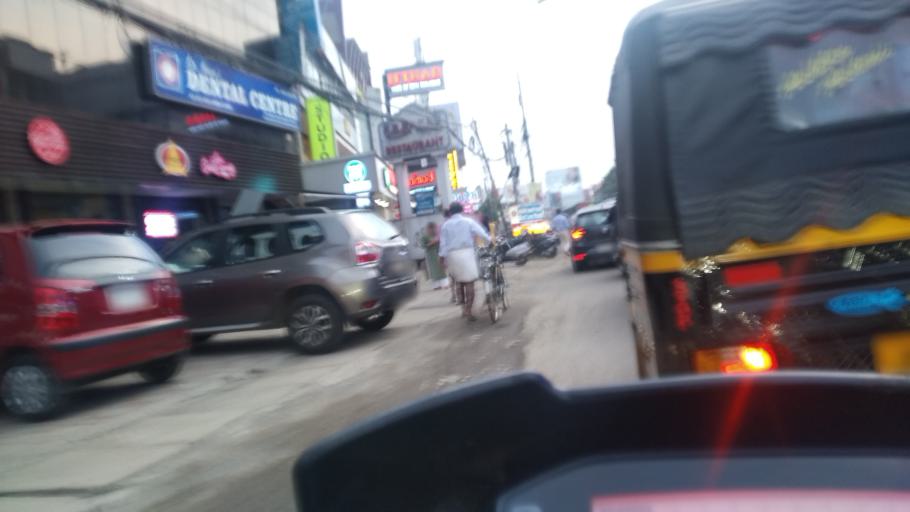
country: IN
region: Kerala
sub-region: Ernakulam
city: Elur
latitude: 10.0034
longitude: 76.3079
